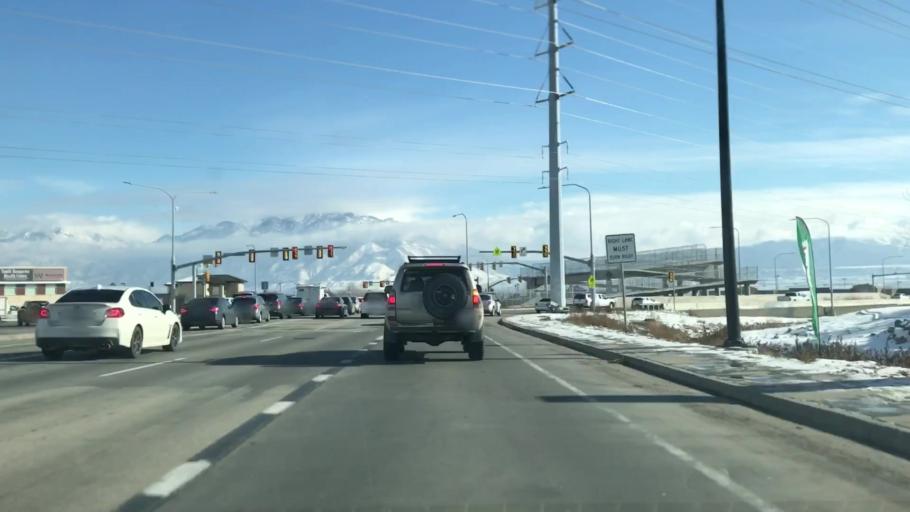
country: US
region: Utah
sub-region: Salt Lake County
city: Riverton
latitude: 40.5077
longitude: -111.9842
